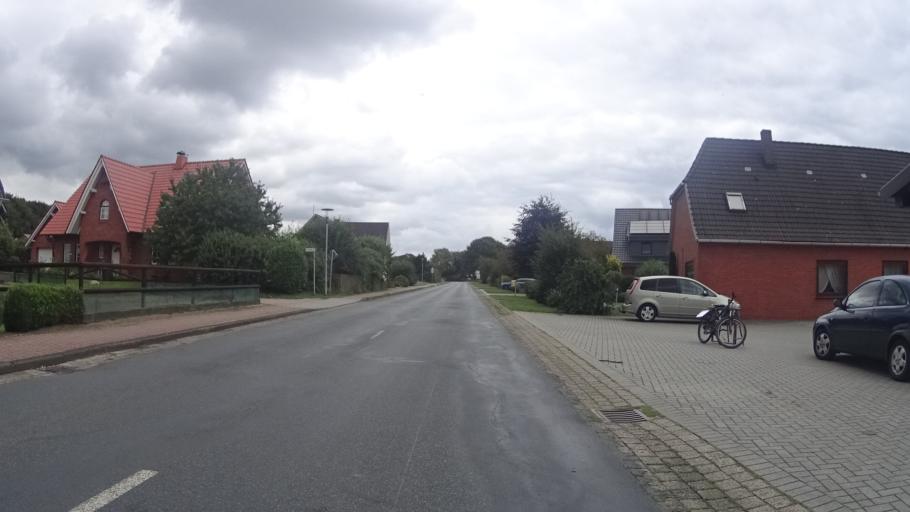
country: DE
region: Lower Saxony
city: Kuhrstedt
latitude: 53.5786
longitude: 8.7863
